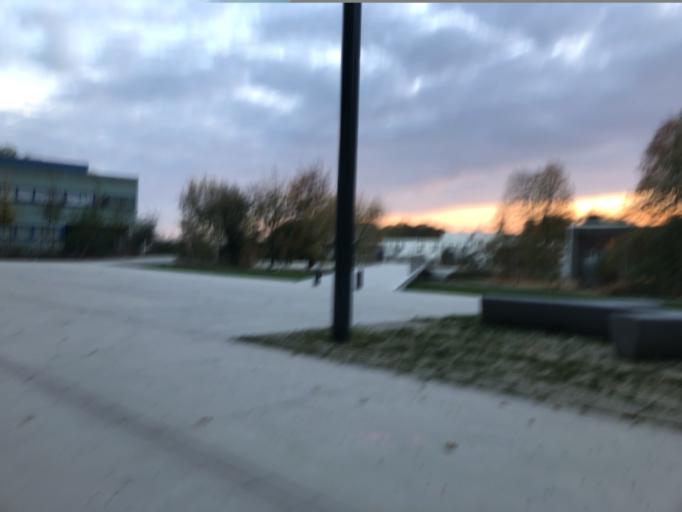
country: FR
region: Ile-de-France
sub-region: Departement de l'Essonne
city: Bures-sur-Yvette
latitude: 48.7105
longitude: 2.1690
